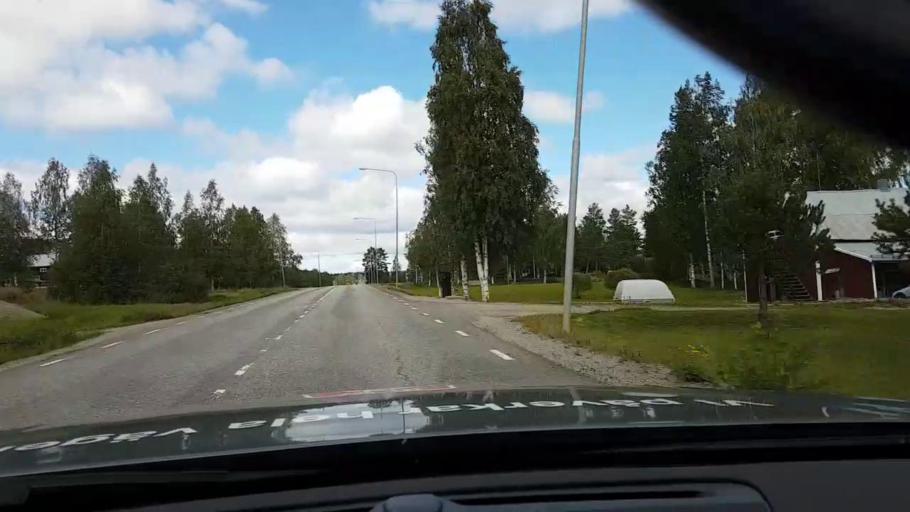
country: SE
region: Vaesternorrland
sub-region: OErnskoeldsviks Kommun
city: Bredbyn
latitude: 63.4754
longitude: 18.0955
